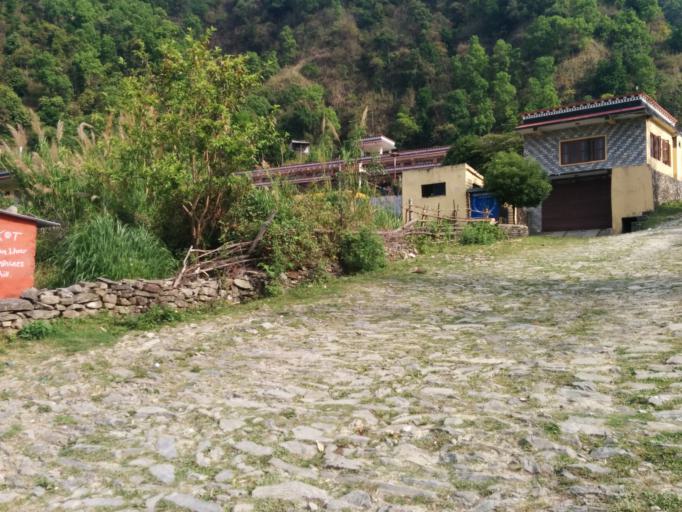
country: NP
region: Western Region
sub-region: Gandaki Zone
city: Pokhara
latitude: 28.2299
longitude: 83.9490
